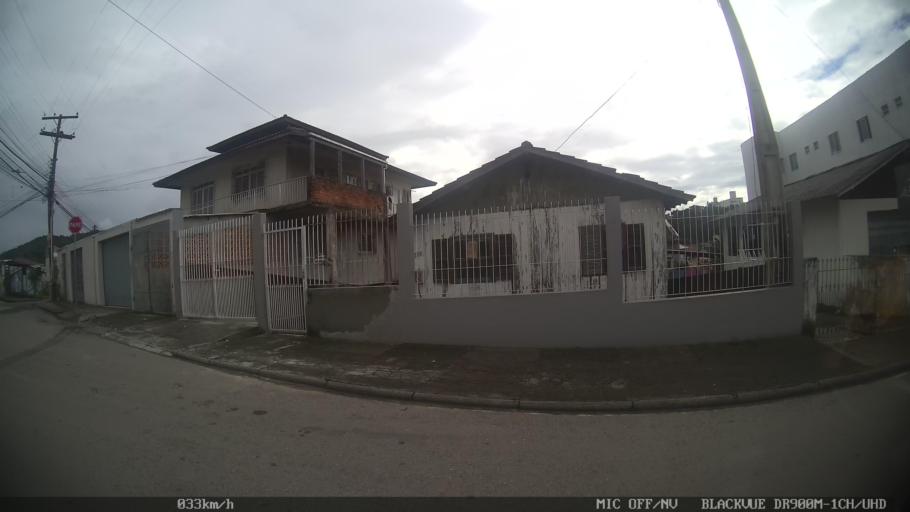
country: BR
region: Santa Catarina
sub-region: Sao Jose
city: Campinas
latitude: -27.5496
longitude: -48.6323
